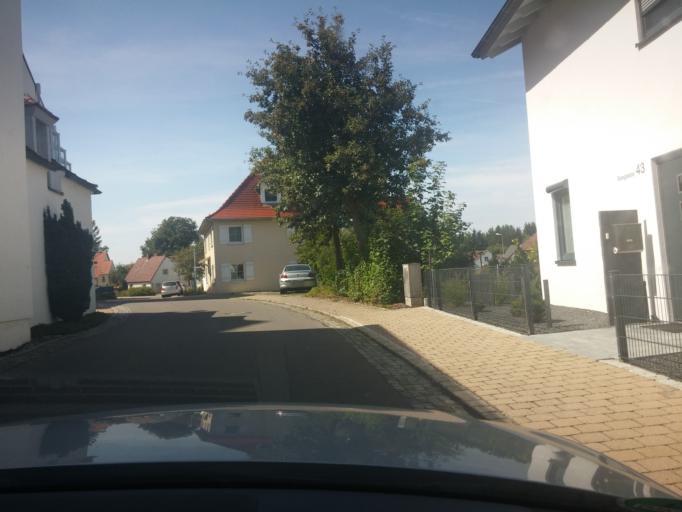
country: DE
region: Baden-Wuerttemberg
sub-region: Tuebingen Region
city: Bad Buchau
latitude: 48.0680
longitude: 9.6117
